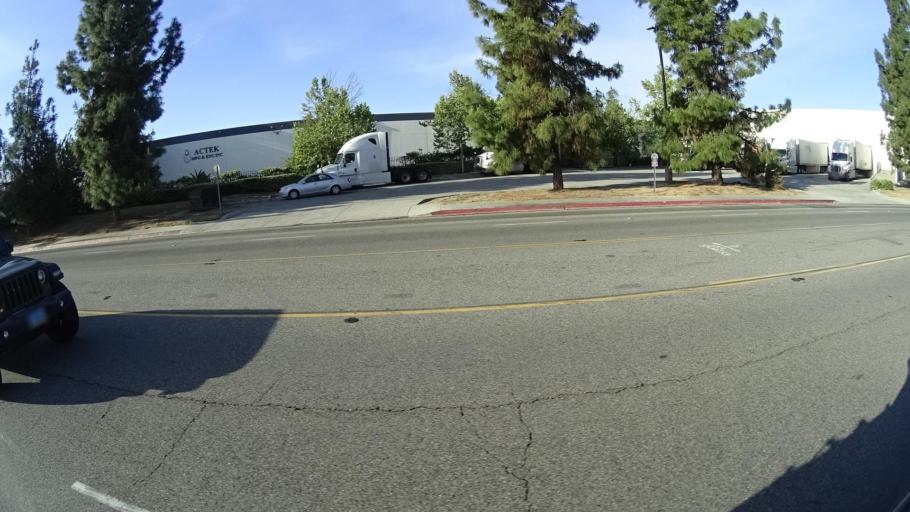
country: US
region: California
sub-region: Los Angeles County
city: South San Jose Hills
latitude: 33.9999
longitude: -117.9026
